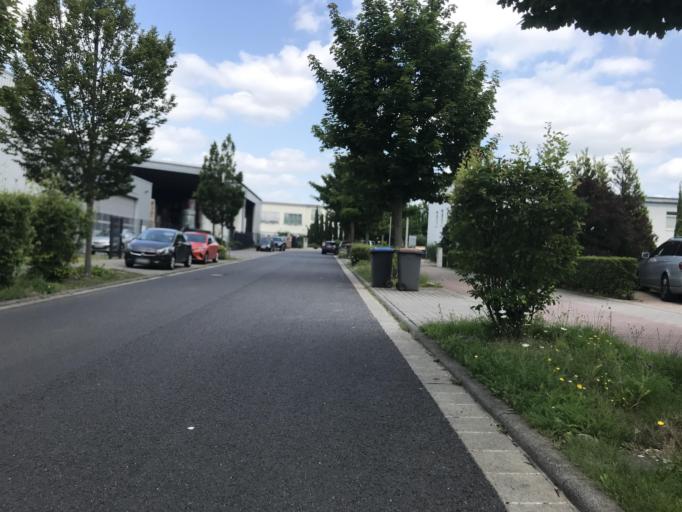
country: DE
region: Hesse
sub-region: Regierungsbezirk Darmstadt
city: Hochheim am Main
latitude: 50.0151
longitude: 8.3731
